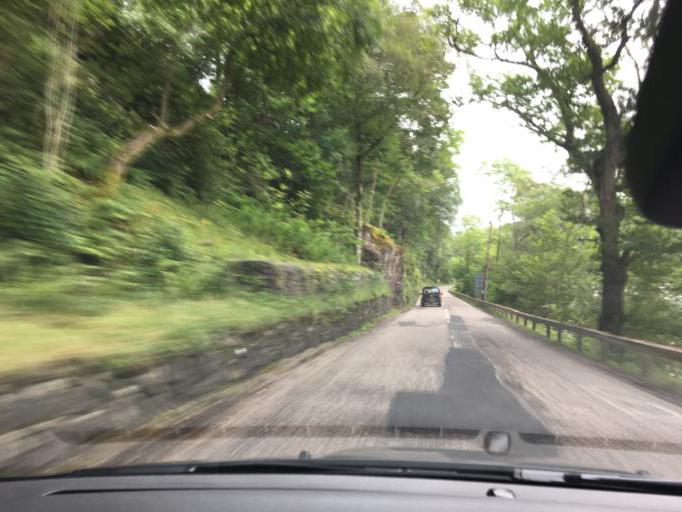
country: GB
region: Scotland
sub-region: Argyll and Bute
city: Garelochhead
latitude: 56.2607
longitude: -4.7040
